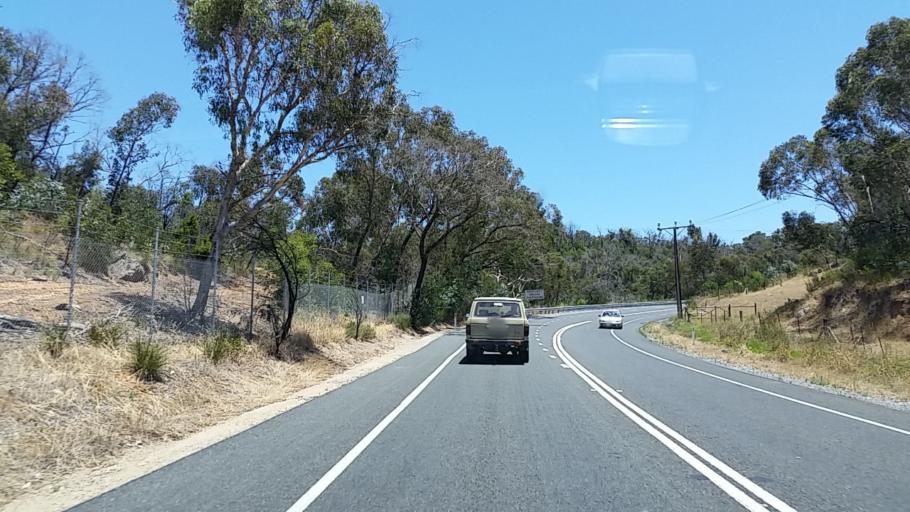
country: AU
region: South Australia
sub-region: Tea Tree Gully
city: Golden Grove
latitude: -34.8187
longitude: 138.7988
